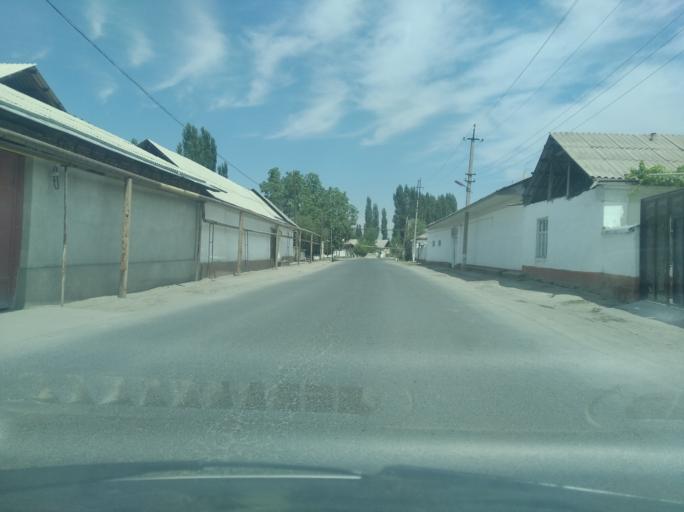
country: UZ
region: Andijon
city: Khujaobod
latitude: 40.6248
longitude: 72.4498
